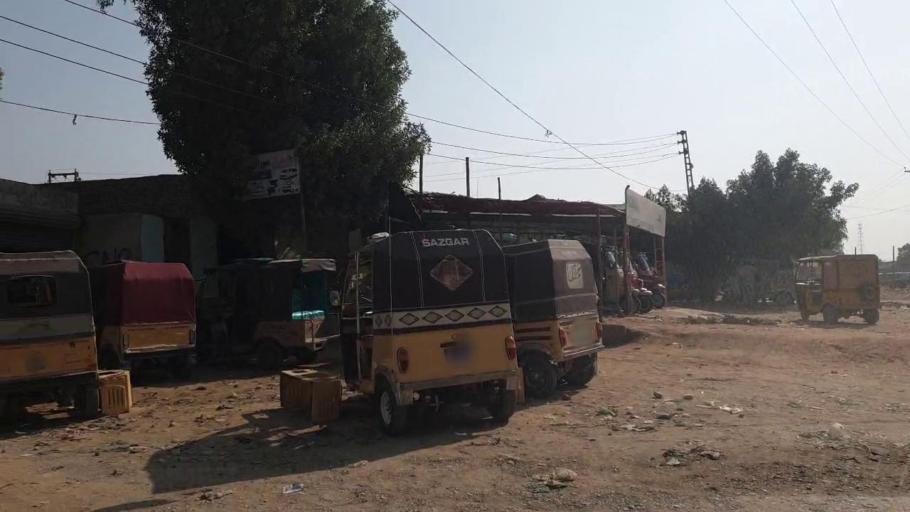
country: PK
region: Sindh
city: Kotri
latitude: 25.3616
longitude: 68.2832
